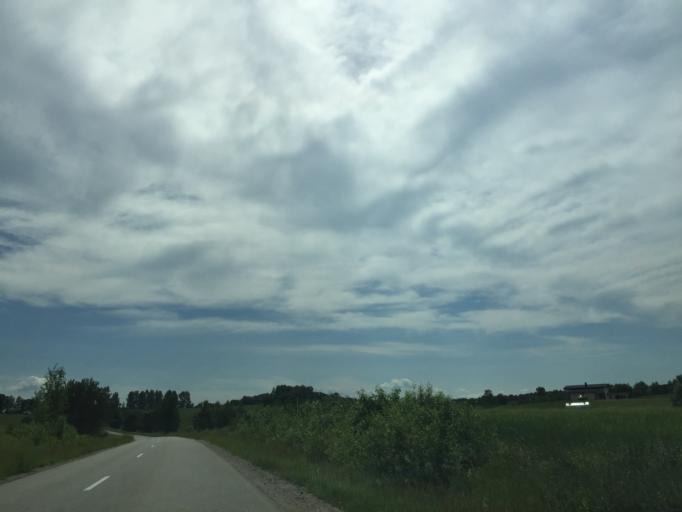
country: LV
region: Engure
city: Smarde
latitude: 57.0376
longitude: 23.2536
